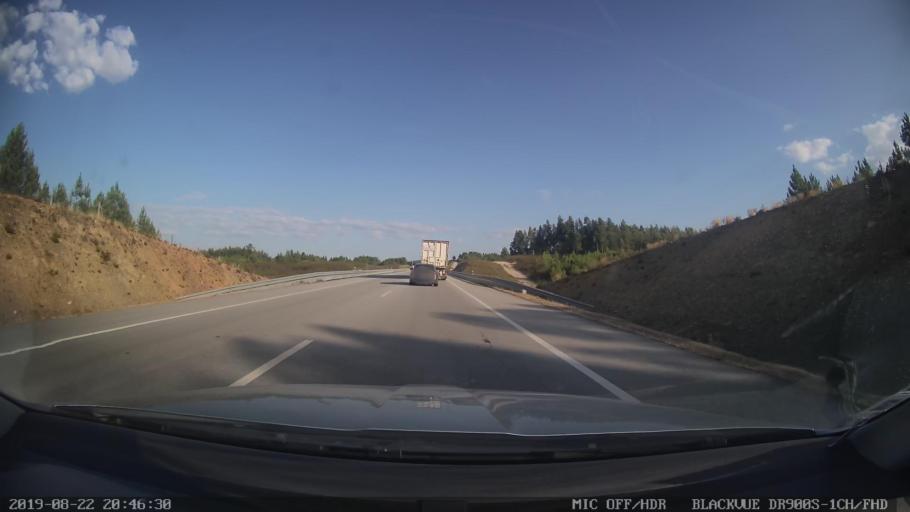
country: PT
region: Castelo Branco
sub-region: Proenca-A-Nova
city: Proenca-a-Nova
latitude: 39.7273
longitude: -7.8772
